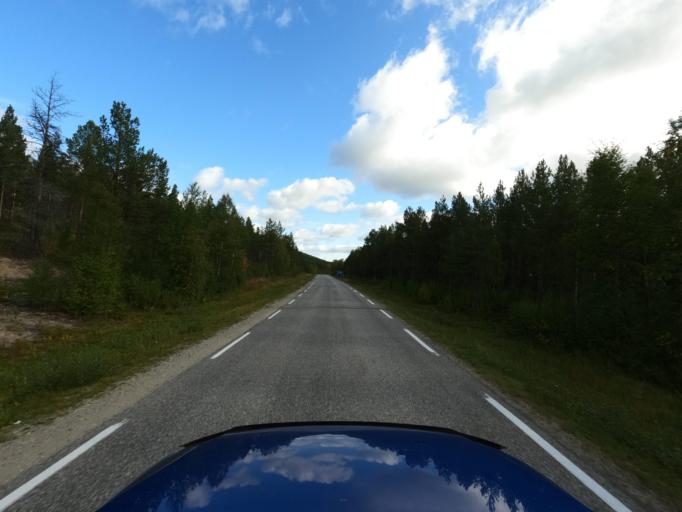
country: NO
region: Finnmark Fylke
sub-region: Karasjok
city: Karasjohka
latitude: 69.4557
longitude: 25.3966
